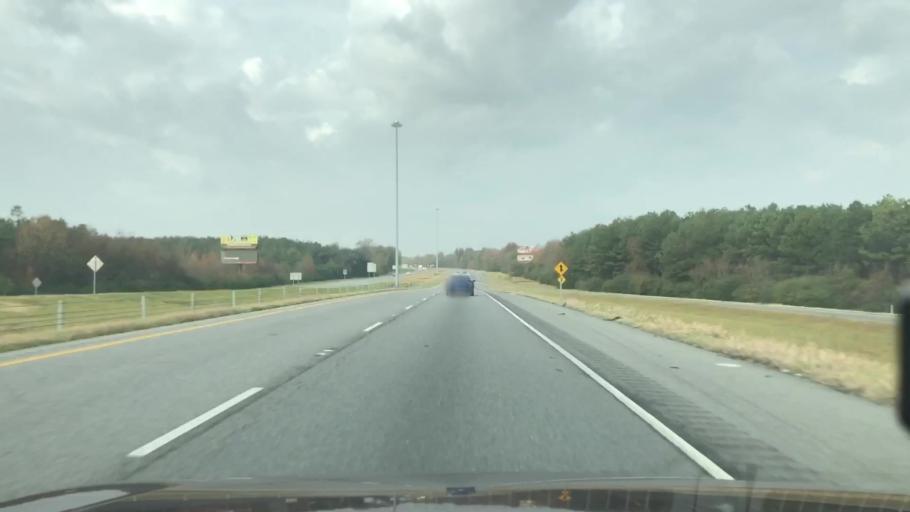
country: US
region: Louisiana
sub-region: Richland Parish
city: Delhi
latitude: 32.4434
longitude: -91.4952
